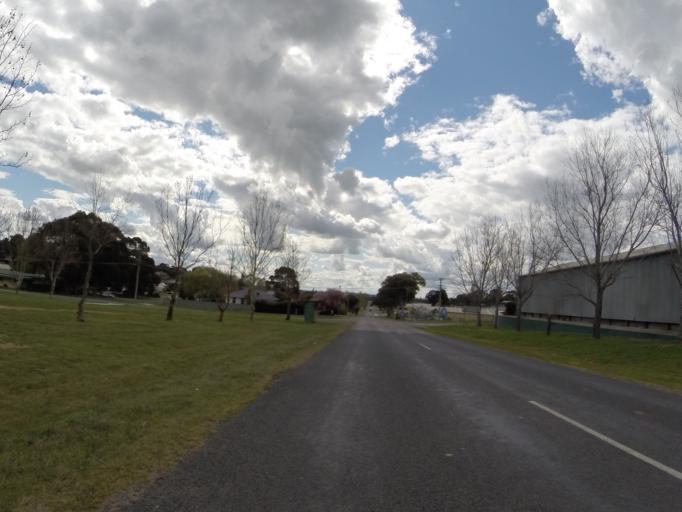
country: AU
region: New South Wales
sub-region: Yass Valley
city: Yass
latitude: -34.8541
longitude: 148.9190
